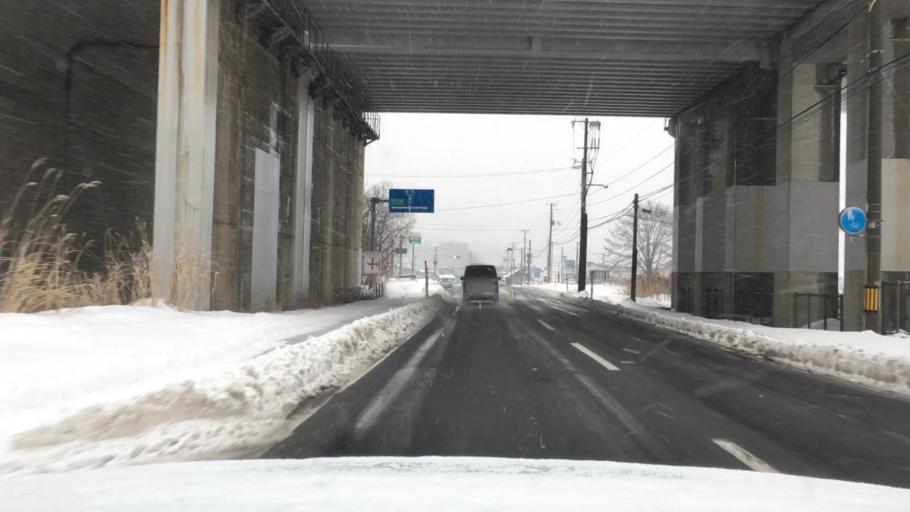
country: JP
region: Iwate
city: Ichinohe
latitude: 40.1089
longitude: 141.0516
